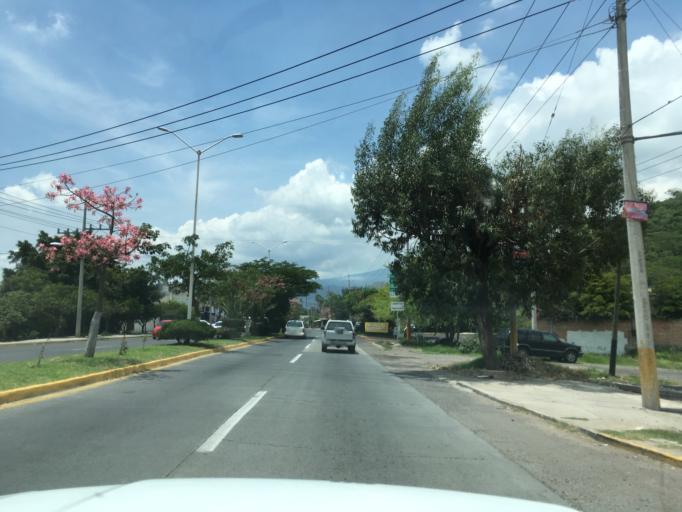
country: MX
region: Jalisco
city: Tlajomulco de Zuniga
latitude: 20.4786
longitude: -103.4537
